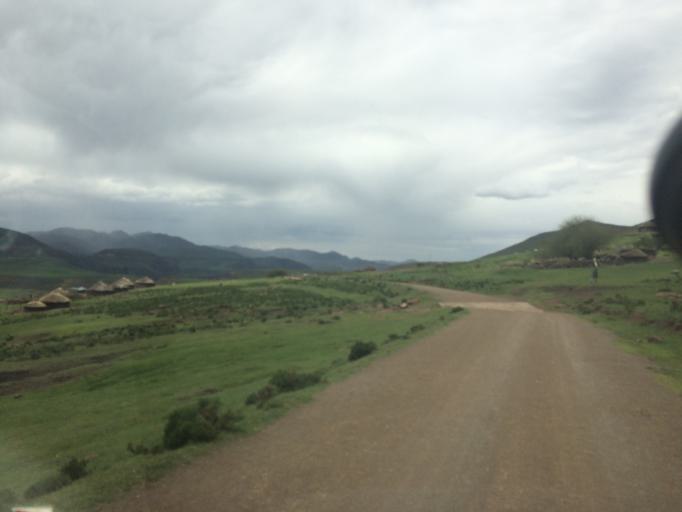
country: LS
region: Maseru
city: Nako
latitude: -29.8514
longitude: 28.0286
